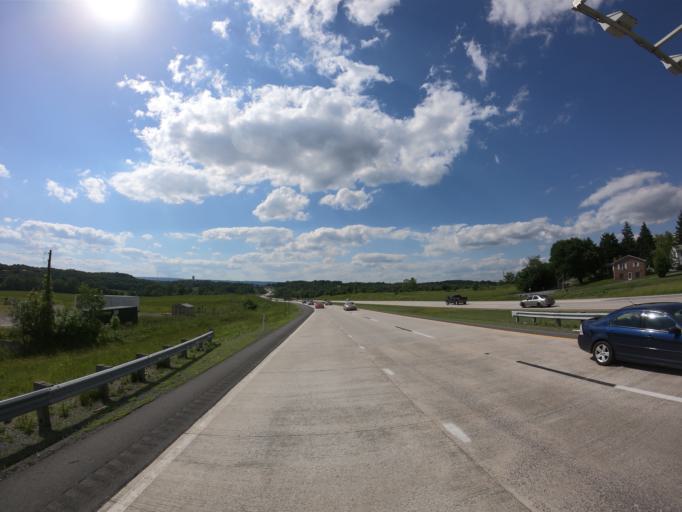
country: US
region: West Virginia
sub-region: Berkeley County
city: Martinsburg
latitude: 39.4217
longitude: -77.9316
